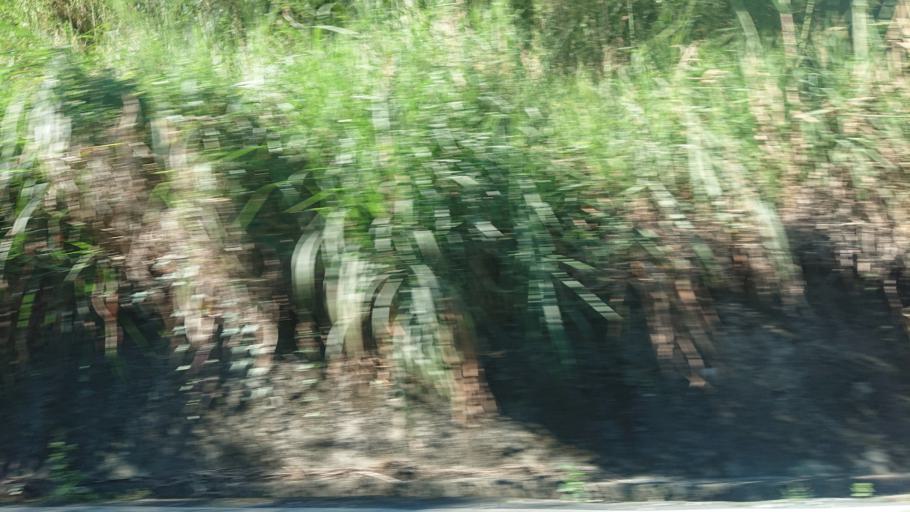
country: TW
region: Taiwan
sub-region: Yunlin
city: Douliu
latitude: 23.5323
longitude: 120.6613
